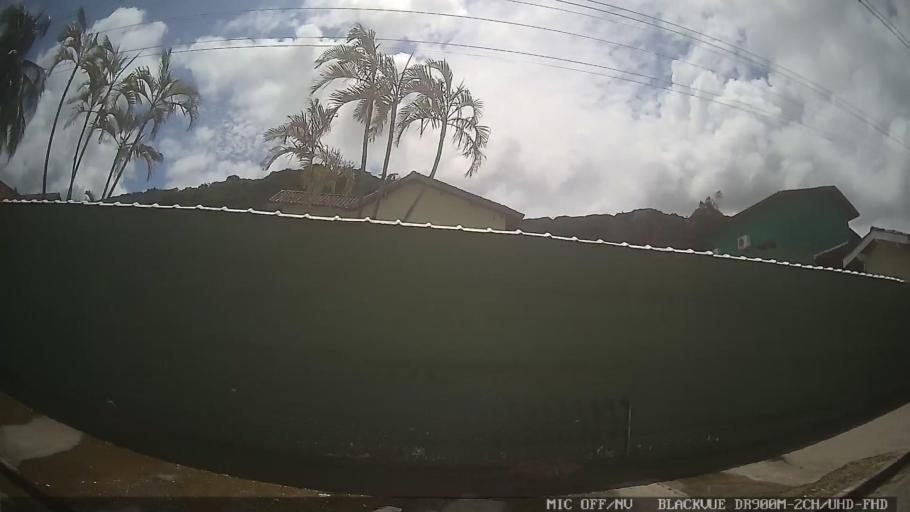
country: BR
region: Sao Paulo
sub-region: Caraguatatuba
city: Caraguatatuba
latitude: -23.6174
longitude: -45.3962
